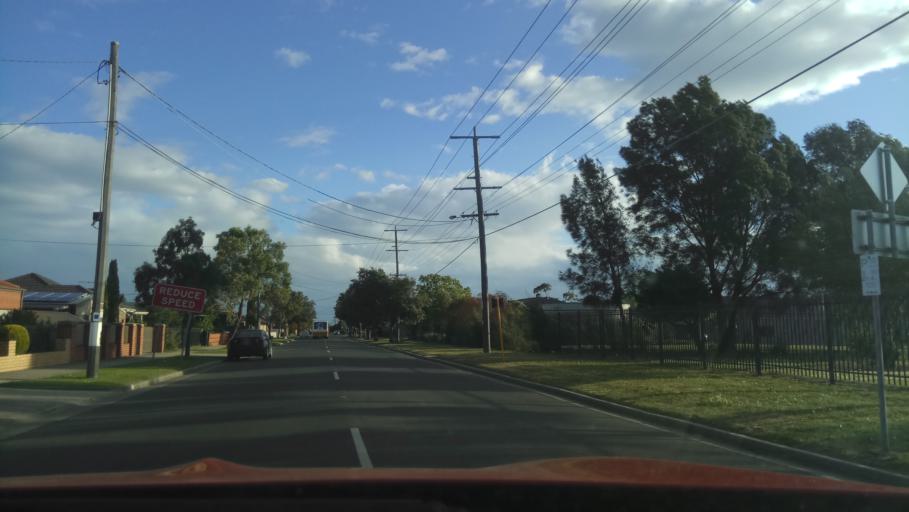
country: AU
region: Victoria
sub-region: Hobsons Bay
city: Altona North
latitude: -37.8333
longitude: 144.8429
